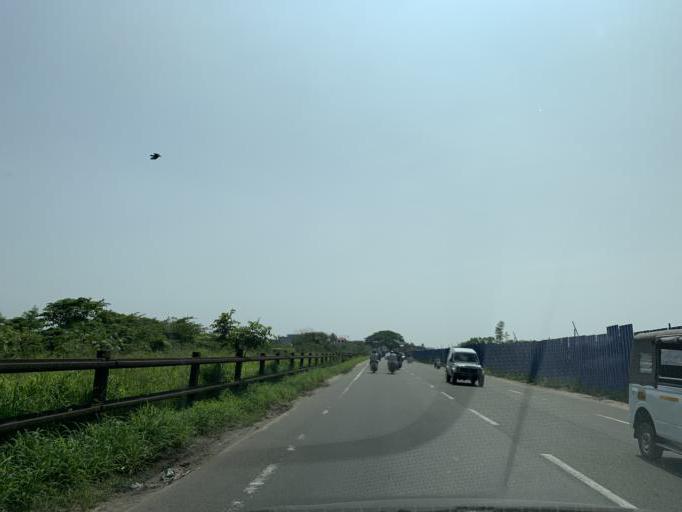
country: IN
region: Kerala
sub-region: Ernakulam
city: Cochin
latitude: 9.9404
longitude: 76.2811
